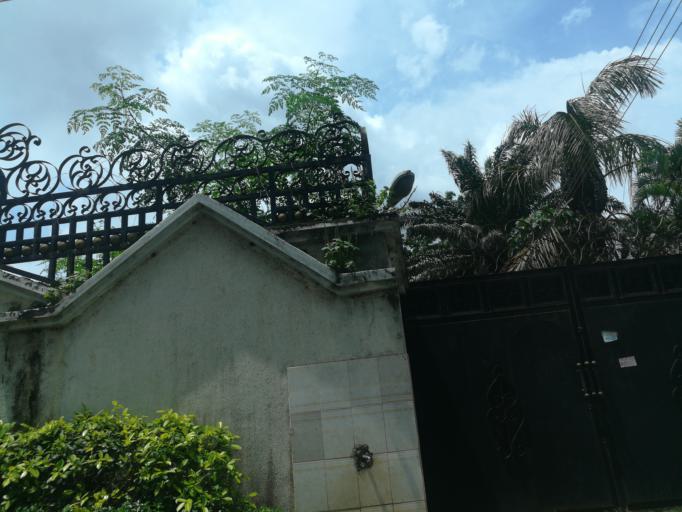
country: NG
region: Lagos
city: Somolu
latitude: 6.5407
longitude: 3.3648
